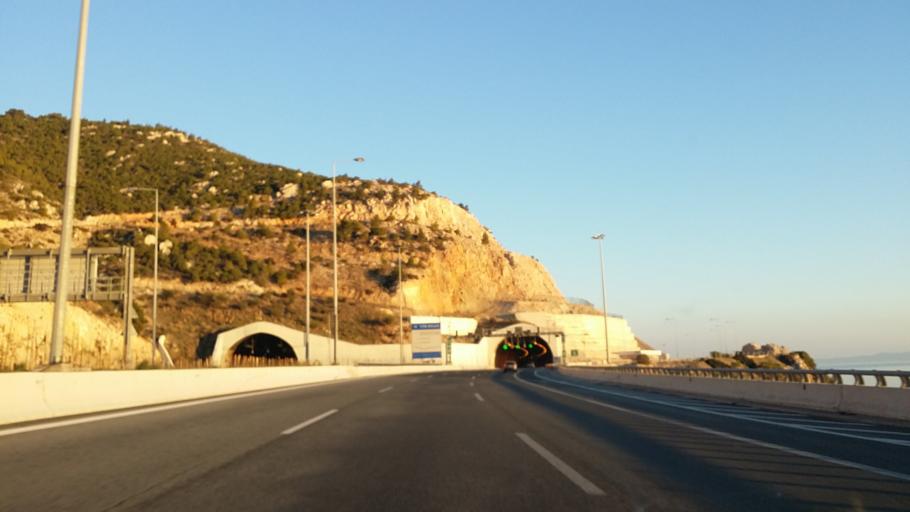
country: GR
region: Attica
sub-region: Nomarchia Dytikis Attikis
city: Megara
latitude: 37.9755
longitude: 23.2901
